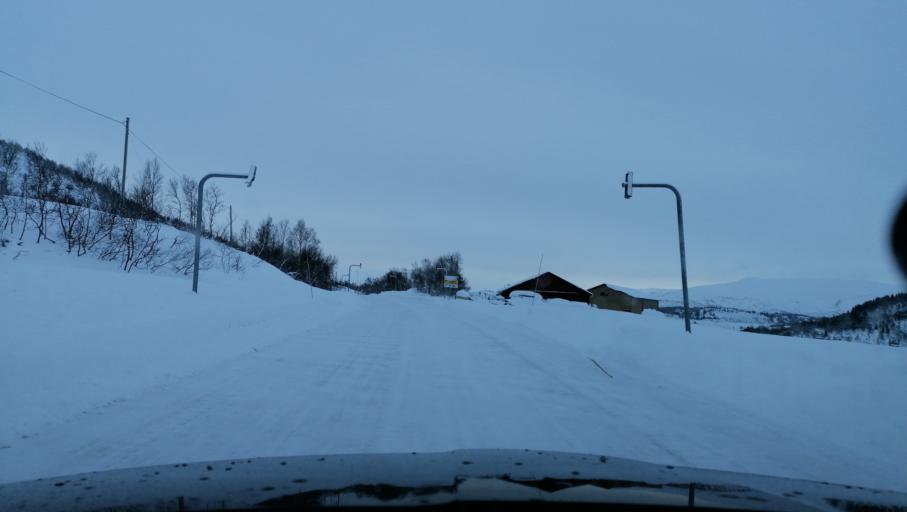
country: NO
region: Aust-Agder
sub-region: Bykle
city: Hovden
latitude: 59.6439
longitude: 7.4596
